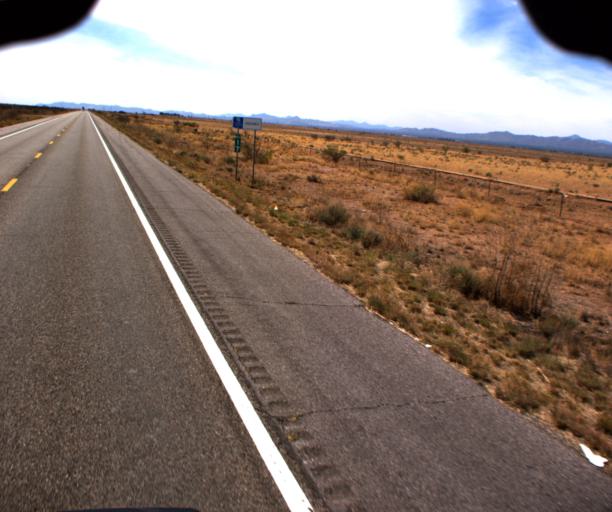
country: US
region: Arizona
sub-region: Cochise County
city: Pirtleville
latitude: 31.5796
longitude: -109.6686
